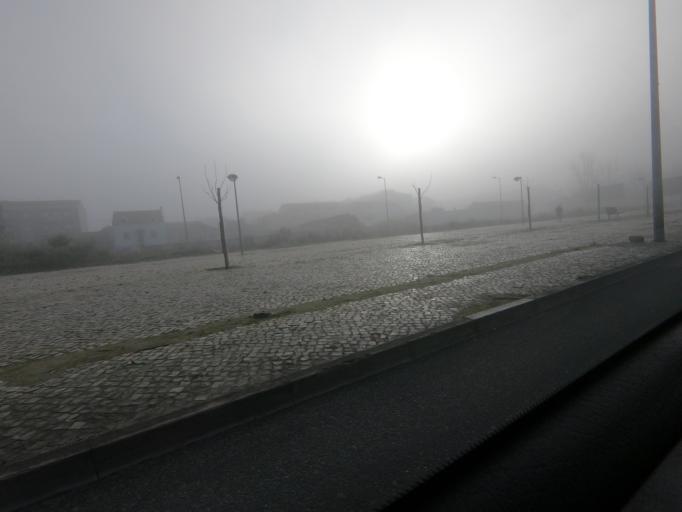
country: PT
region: Setubal
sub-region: Palmela
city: Pinhal Novo
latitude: 38.6285
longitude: -8.9177
